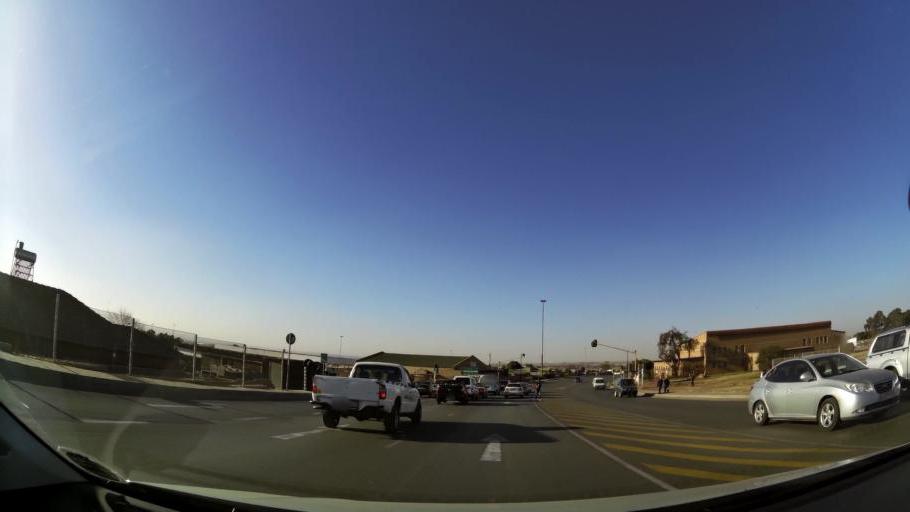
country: ZA
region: Gauteng
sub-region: Ekurhuleni Metropolitan Municipality
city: Tembisa
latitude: -26.0014
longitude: 28.2223
